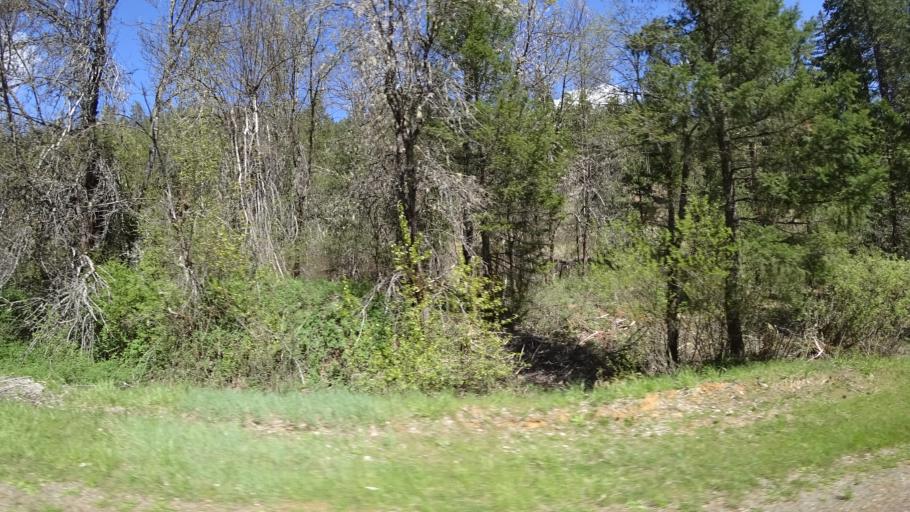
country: US
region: California
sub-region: Trinity County
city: Weaverville
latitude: 40.7716
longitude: -122.8915
